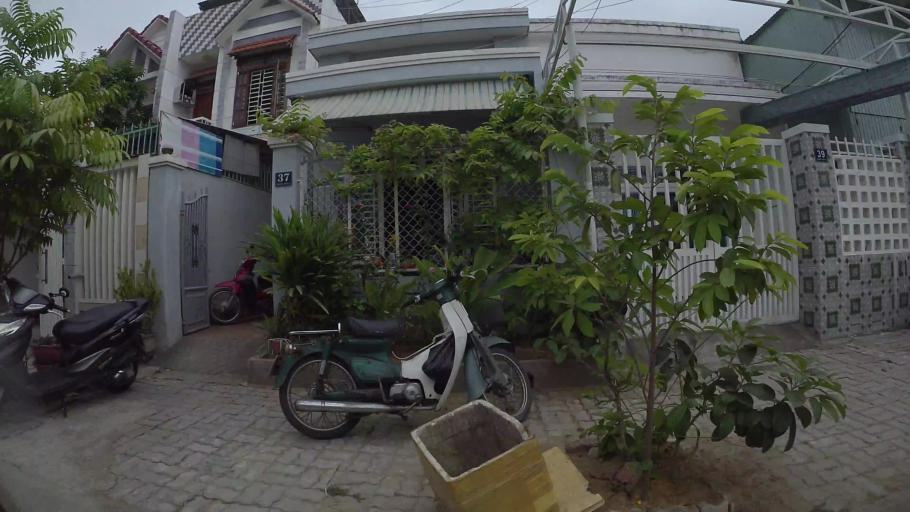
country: VN
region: Da Nang
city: Lien Chieu
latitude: 16.0468
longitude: 108.1727
